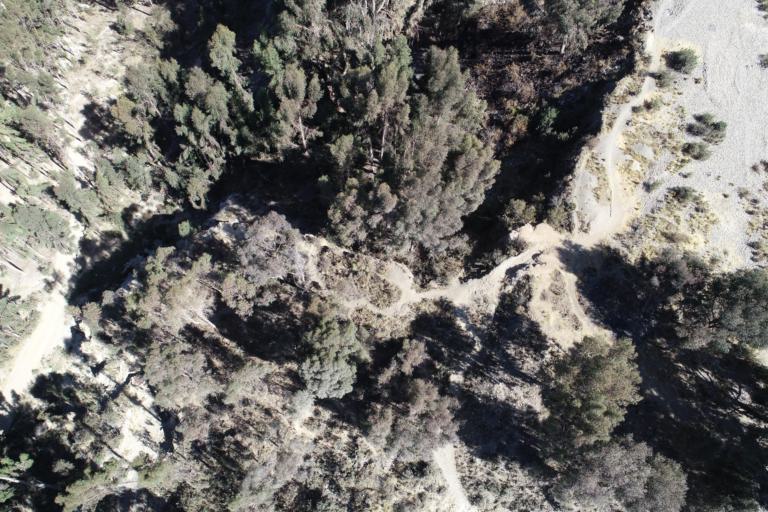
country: BO
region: La Paz
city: La Paz
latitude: -16.5418
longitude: -68.1540
